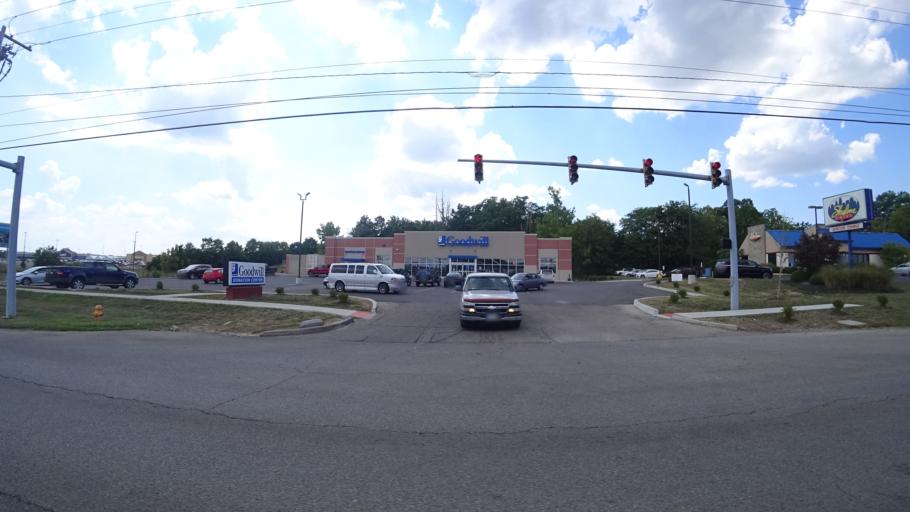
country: US
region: Ohio
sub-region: Butler County
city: Hamilton
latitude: 39.4287
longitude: -84.5990
